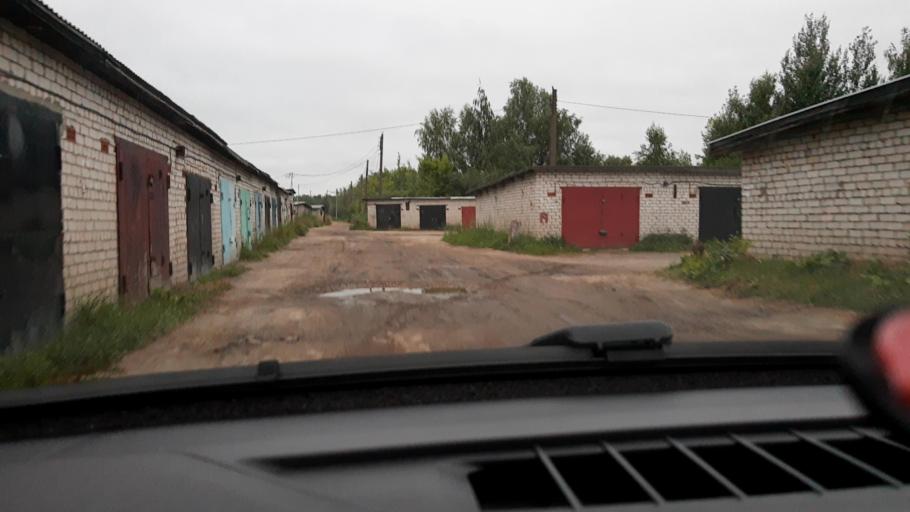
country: RU
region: Nizjnij Novgorod
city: Gorbatovka
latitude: 56.3088
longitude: 43.8161
